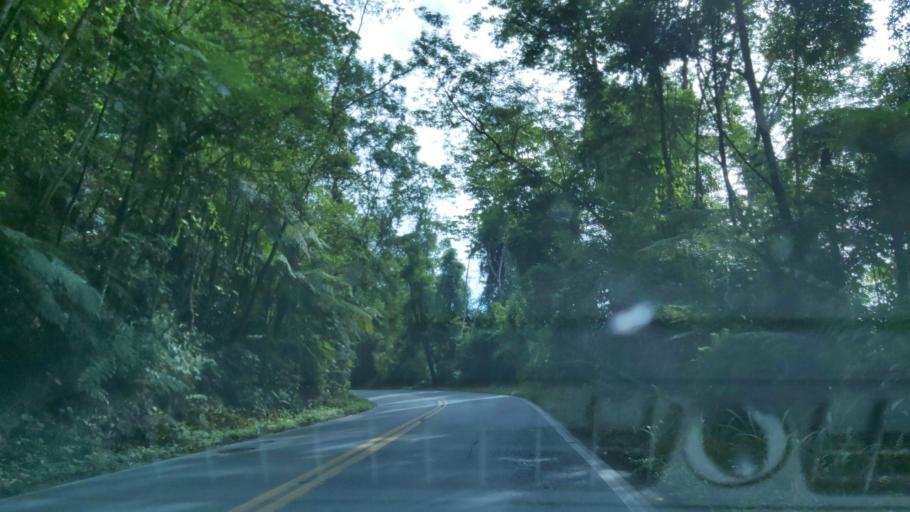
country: BR
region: Sao Paulo
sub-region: Juquia
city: Juquia
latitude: -24.0980
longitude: -47.6176
